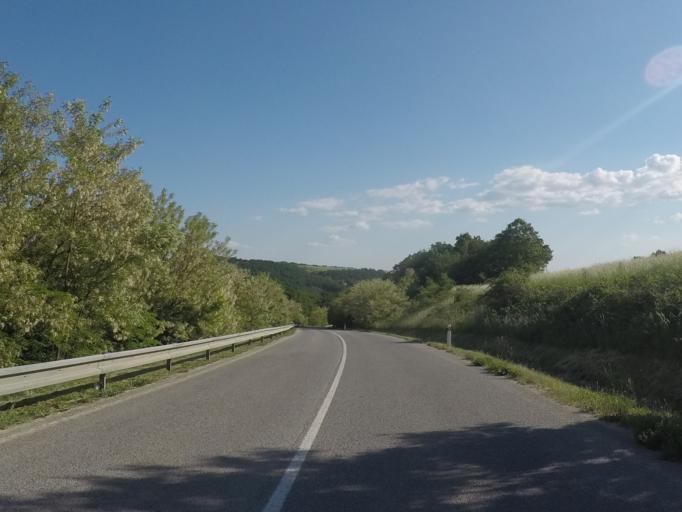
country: SK
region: Kosicky
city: Roznava
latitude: 48.5326
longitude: 20.4107
